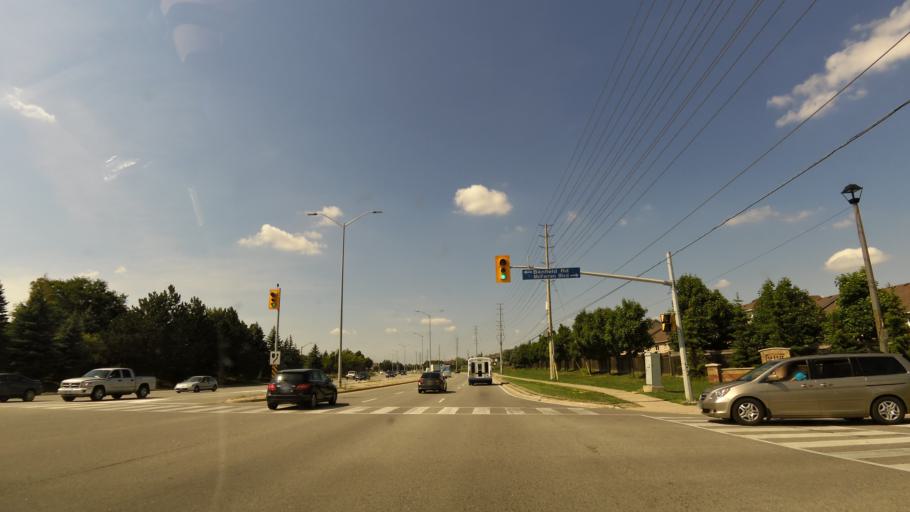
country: CA
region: Ontario
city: Mississauga
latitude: 43.5677
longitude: -79.7186
